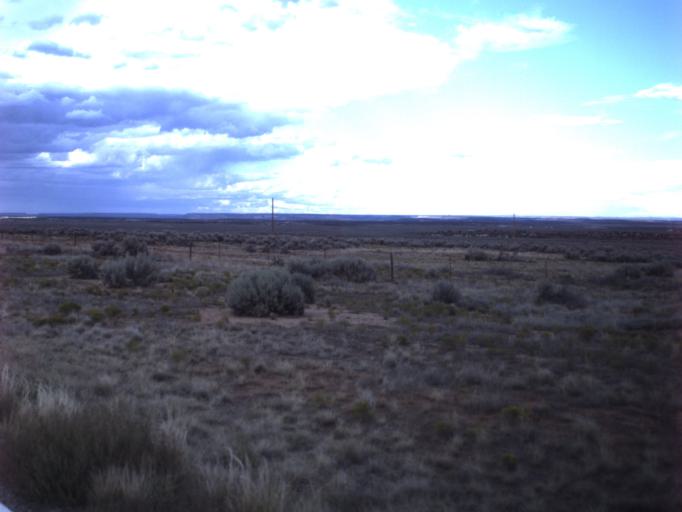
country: US
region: Utah
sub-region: San Juan County
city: Blanding
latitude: 37.3924
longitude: -109.3391
